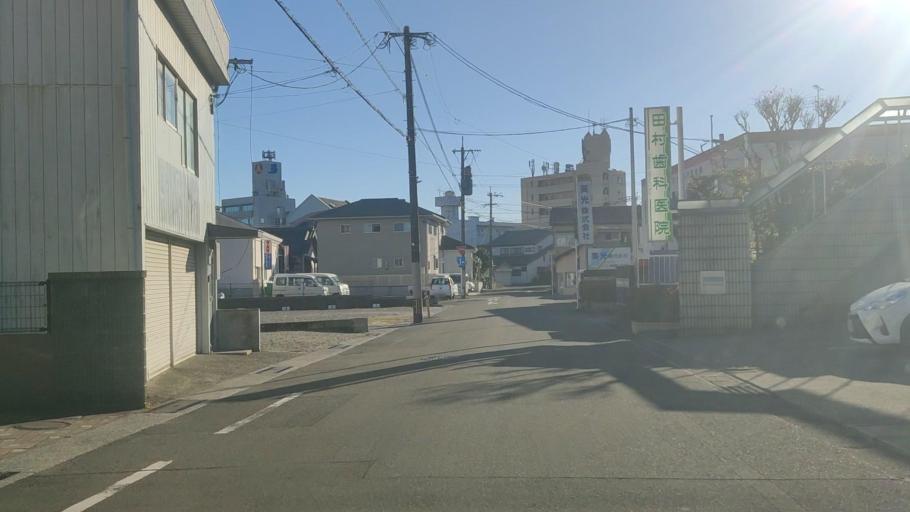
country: JP
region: Miyazaki
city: Miyazaki-shi
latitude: 31.8996
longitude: 131.4241
